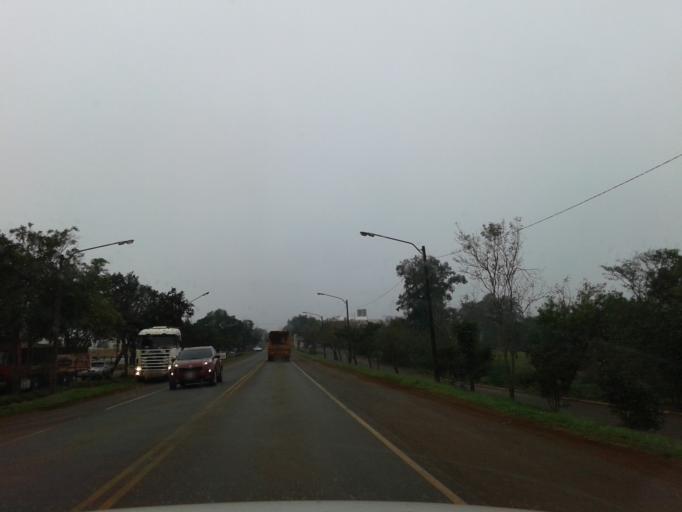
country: PY
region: Alto Parana
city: Santa Rita
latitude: -25.8054
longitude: -55.0973
